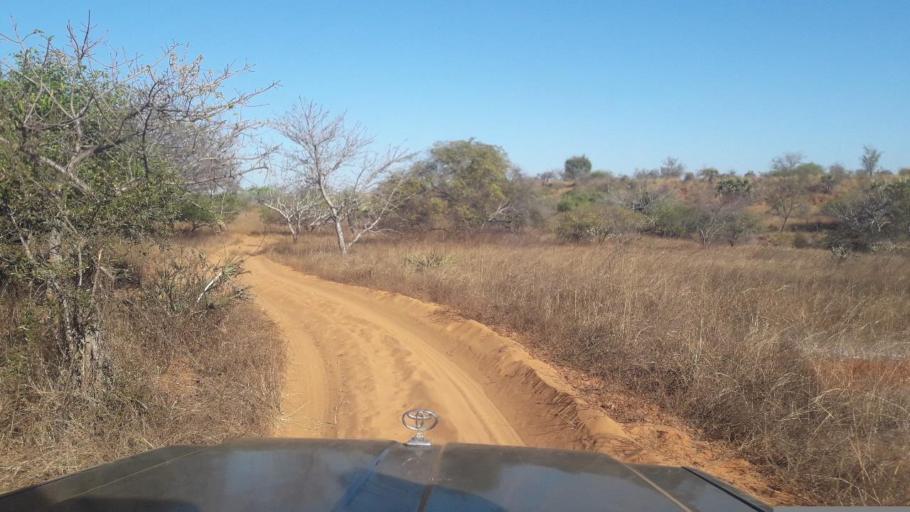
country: MG
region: Boeny
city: Sitampiky
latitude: -16.4170
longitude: 45.6098
